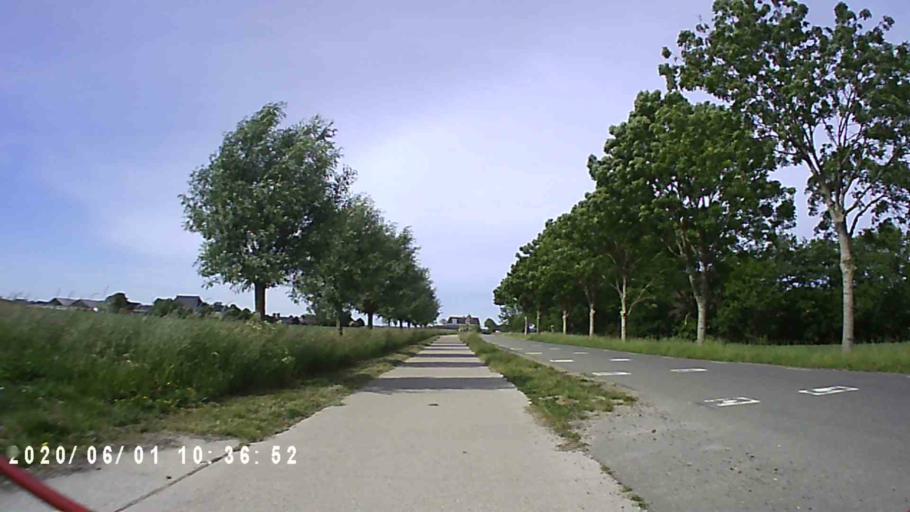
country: NL
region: Friesland
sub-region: Gemeente Het Bildt
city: Minnertsga
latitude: 53.2215
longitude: 5.5862
